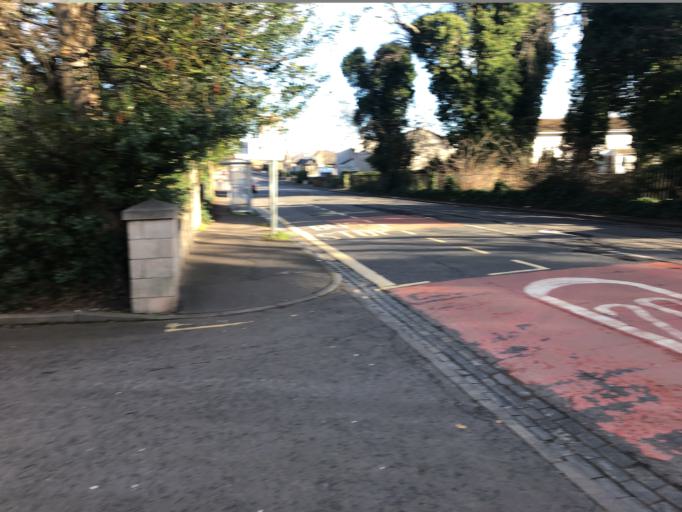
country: GB
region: Scotland
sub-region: West Lothian
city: Seafield
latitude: 55.9458
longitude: -3.1348
